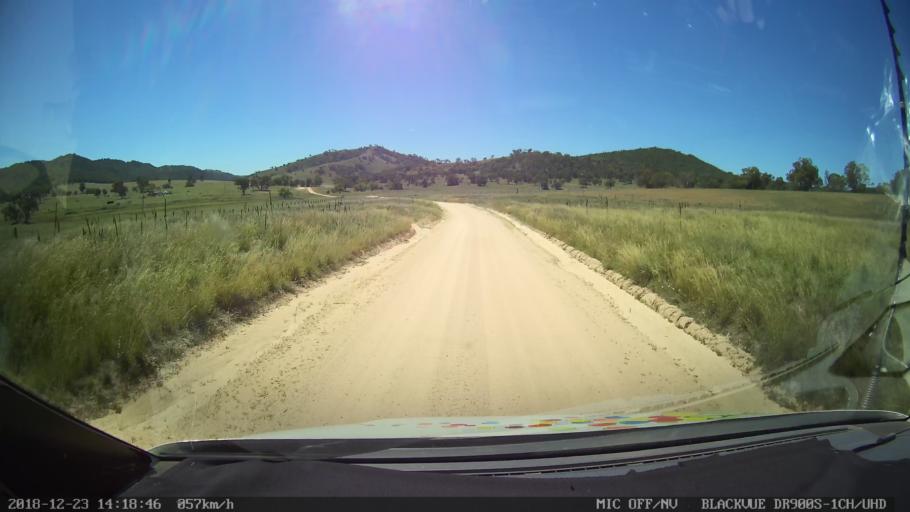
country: AU
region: New South Wales
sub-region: Tamworth Municipality
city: Manilla
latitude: -30.6562
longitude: 151.0008
